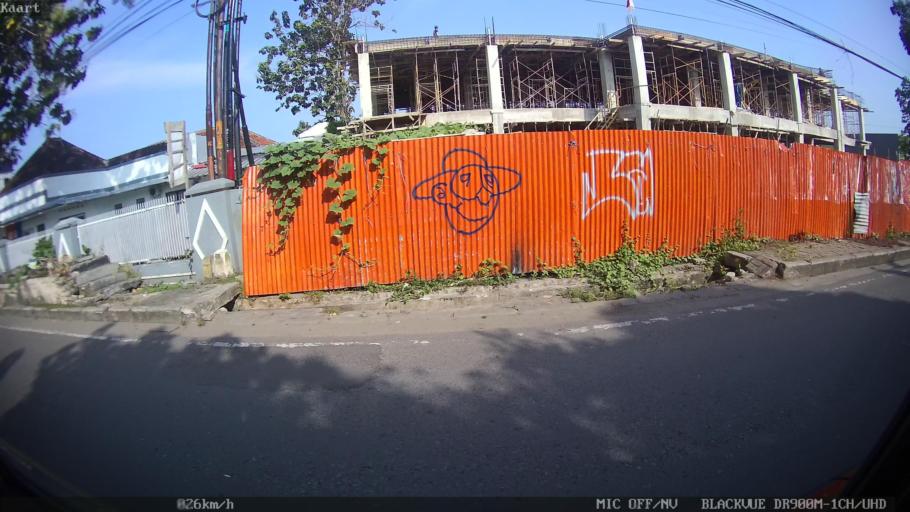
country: ID
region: Lampung
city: Bandarlampung
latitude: -5.4072
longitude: 105.2577
